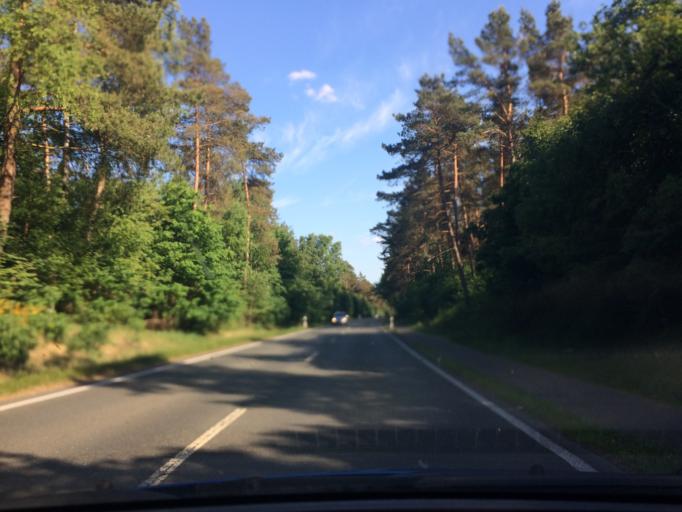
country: DE
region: Lower Saxony
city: Soltau
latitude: 53.0196
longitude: 9.8772
